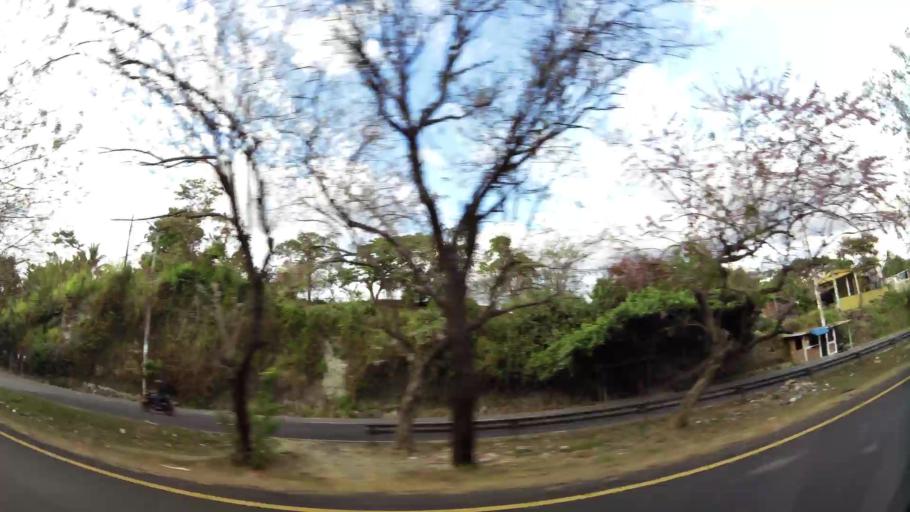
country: SV
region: San Vicente
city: San Sebastian
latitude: 13.7304
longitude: -88.8720
